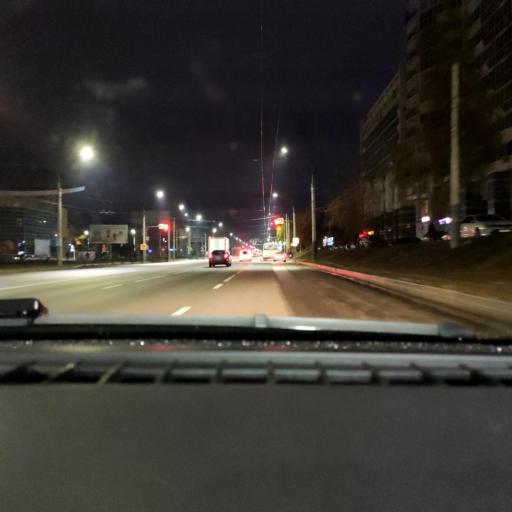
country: RU
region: Voronezj
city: Voronezh
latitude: 51.6628
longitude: 39.2478
